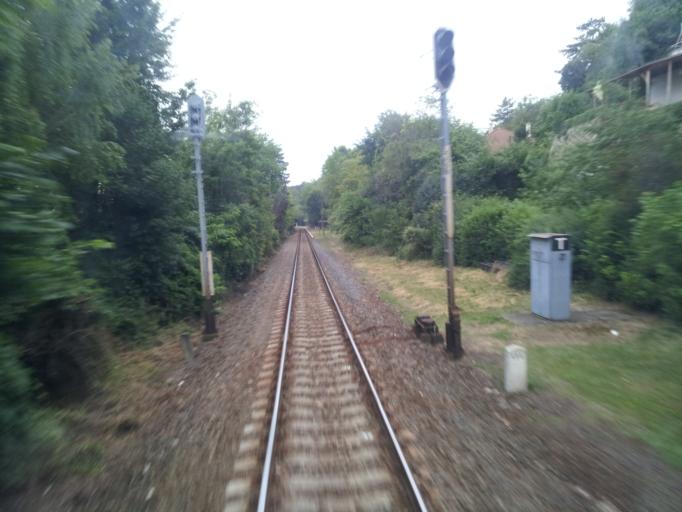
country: HU
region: Veszprem
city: Balatonalmadi
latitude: 47.0122
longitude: 18.0058
